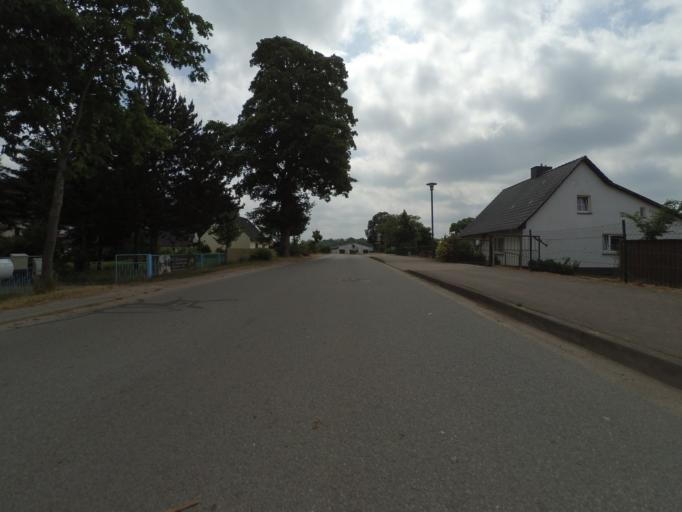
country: DE
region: Mecklenburg-Vorpommern
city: Krakow am See
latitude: 53.6091
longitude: 12.3846
